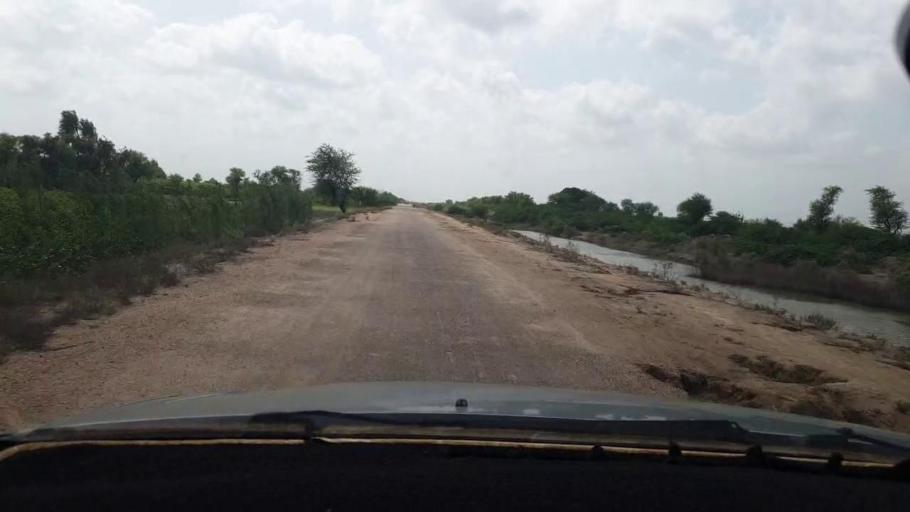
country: PK
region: Sindh
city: Tando Bago
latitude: 24.7283
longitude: 69.1342
